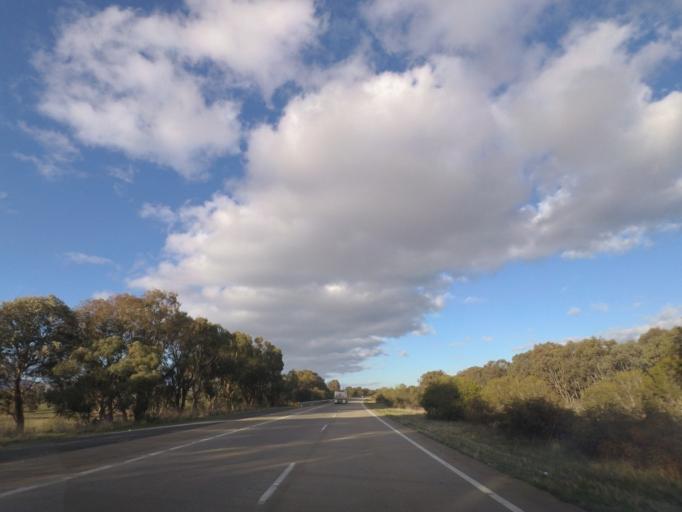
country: AU
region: New South Wales
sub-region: Yass Valley
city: Yass
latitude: -34.8009
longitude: 148.5007
